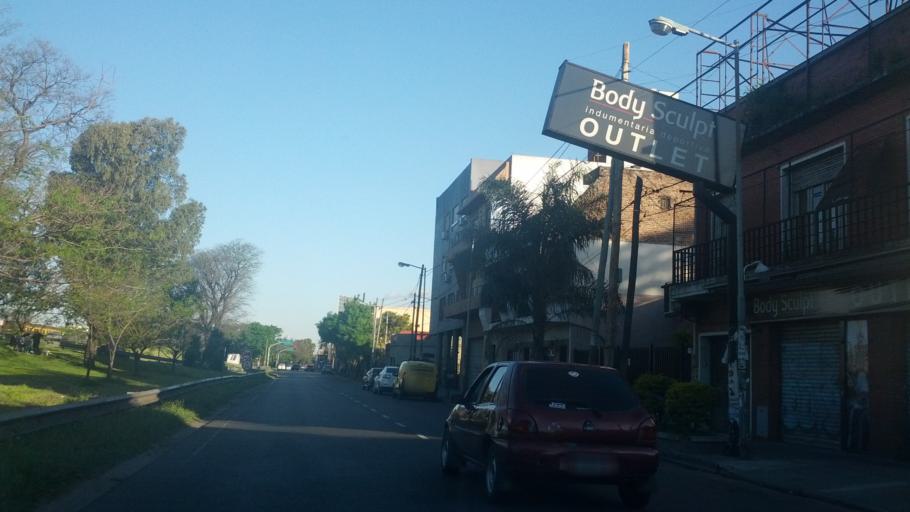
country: AR
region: Buenos Aires
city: San Justo
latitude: -34.6554
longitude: -58.5279
